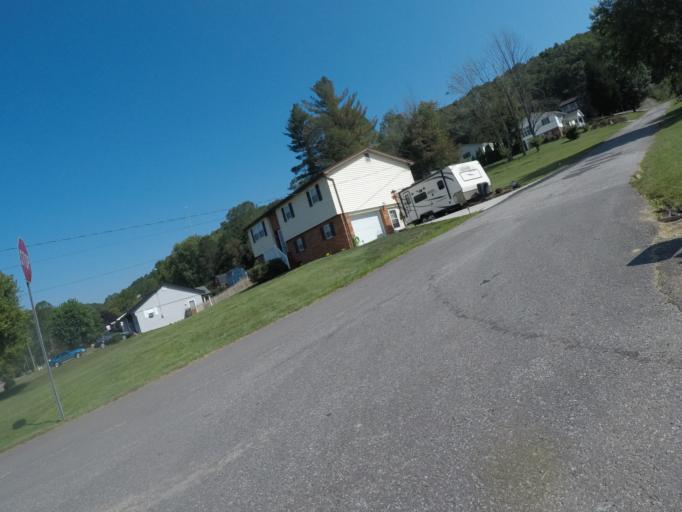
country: US
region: West Virginia
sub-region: Cabell County
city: Barboursville
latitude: 38.3720
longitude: -82.2746
